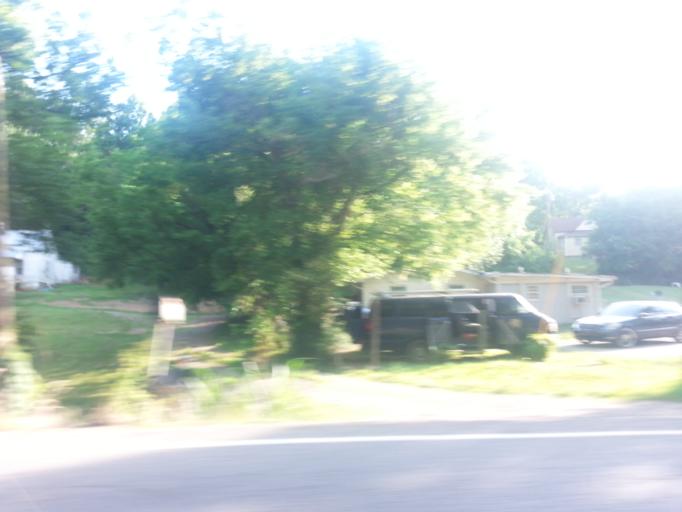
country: US
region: Tennessee
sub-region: Knox County
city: Knoxville
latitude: 35.9261
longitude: -83.9096
